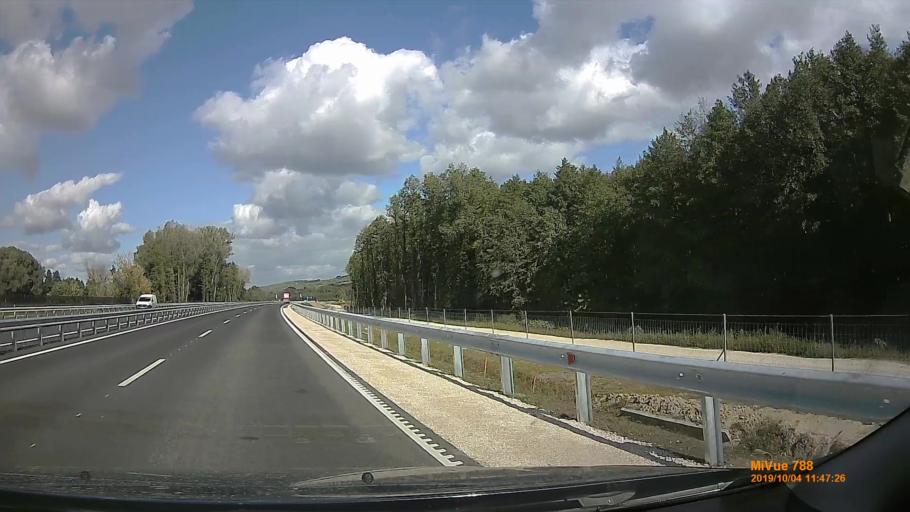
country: HU
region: Somogy
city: Karad
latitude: 46.6490
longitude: 17.7862
